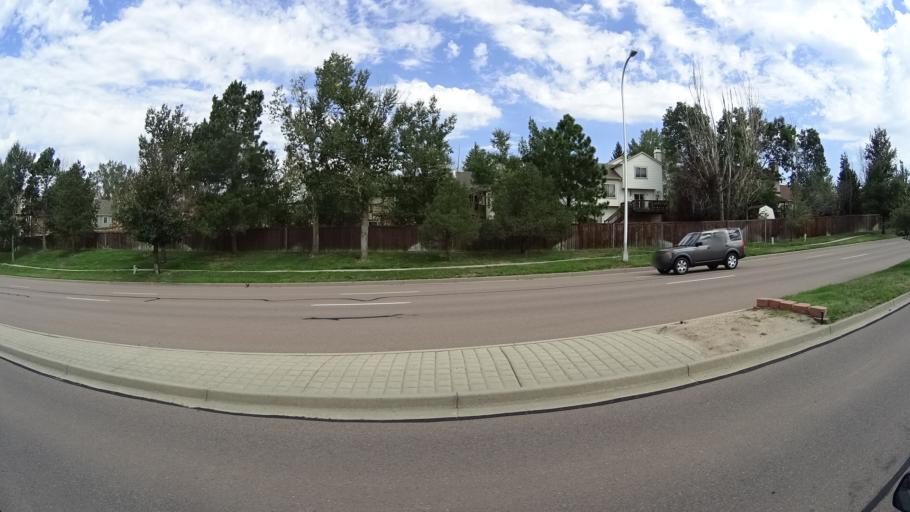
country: US
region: Colorado
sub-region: El Paso County
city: Cimarron Hills
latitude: 38.9022
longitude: -104.7002
